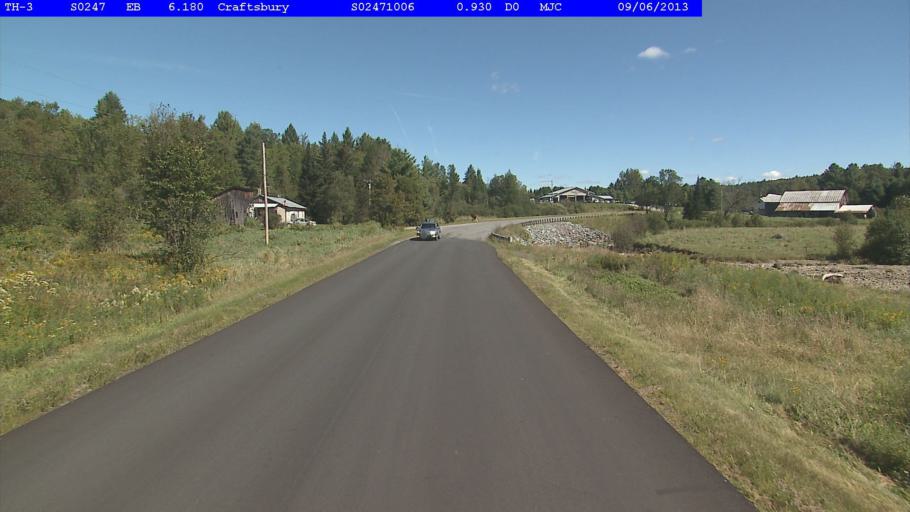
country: US
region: Vermont
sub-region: Caledonia County
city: Hardwick
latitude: 44.6299
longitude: -72.4318
